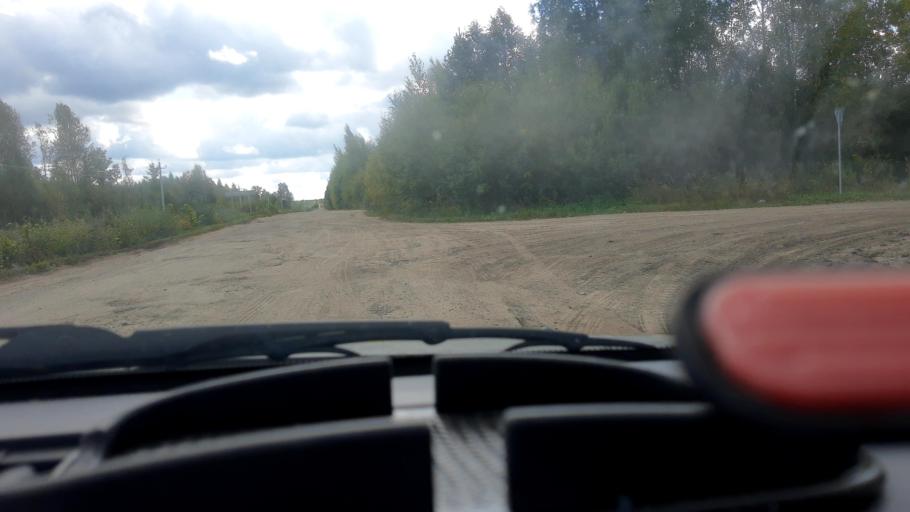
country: RU
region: Mariy-El
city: Kilemary
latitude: 56.8935
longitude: 46.7524
